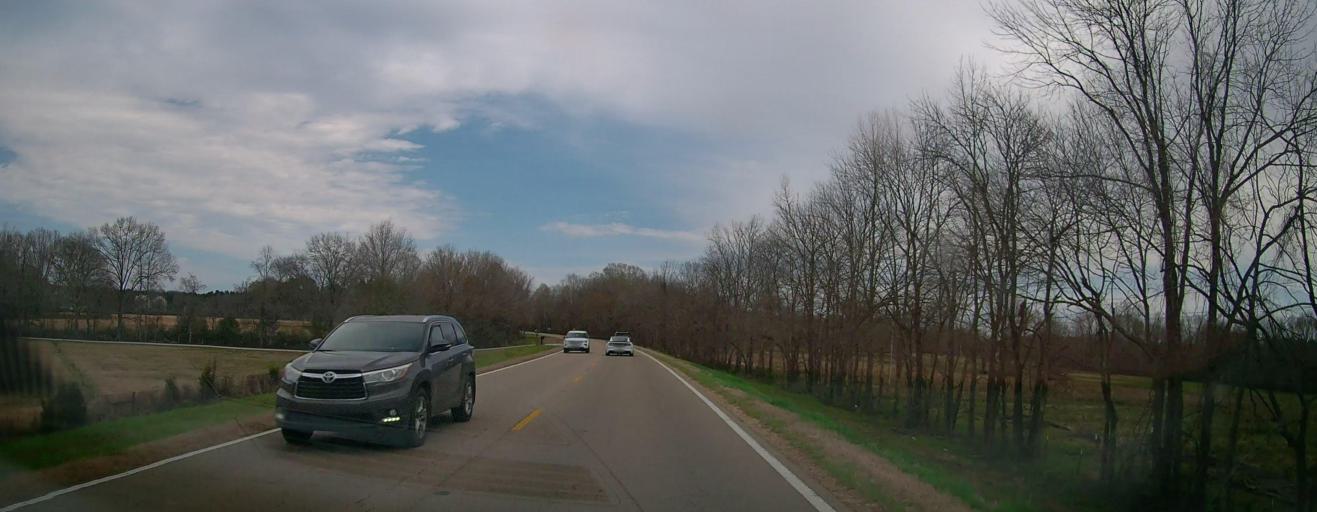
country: US
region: Mississippi
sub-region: Itawamba County
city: Fulton
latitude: 34.2518
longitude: -88.4718
